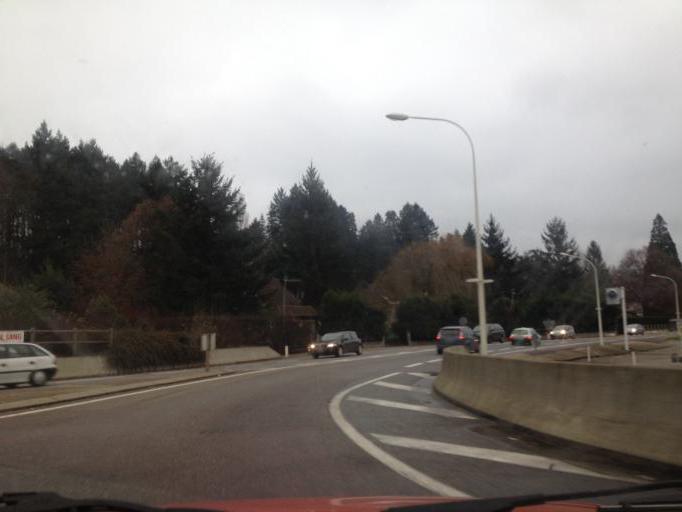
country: FR
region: Auvergne
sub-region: Departement de l'Allier
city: Varennes-sur-Allier
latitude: 46.3258
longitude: 3.3886
